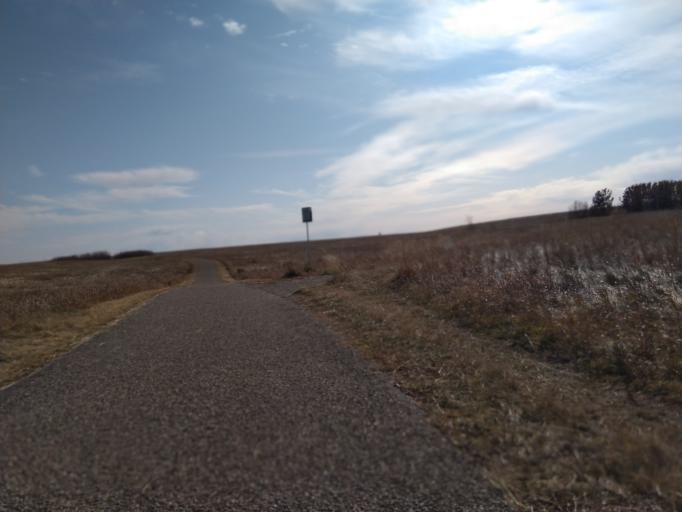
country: CA
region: Alberta
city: Calgary
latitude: 51.1229
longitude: -114.1257
